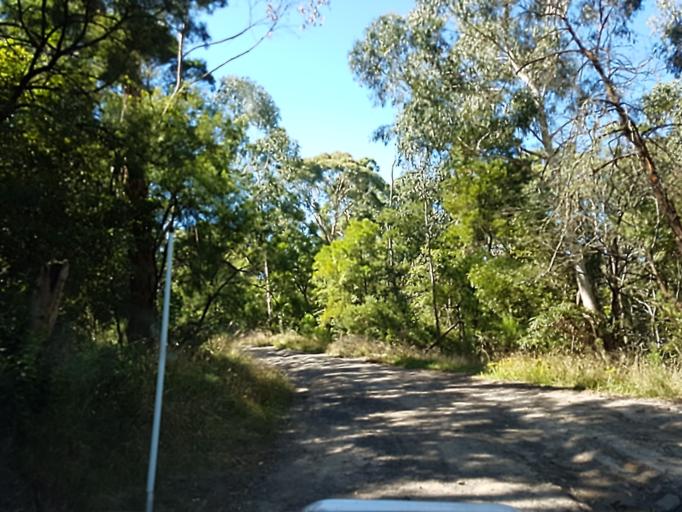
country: AU
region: Victoria
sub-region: Yarra Ranges
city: Tremont
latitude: -37.9071
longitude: 145.3157
